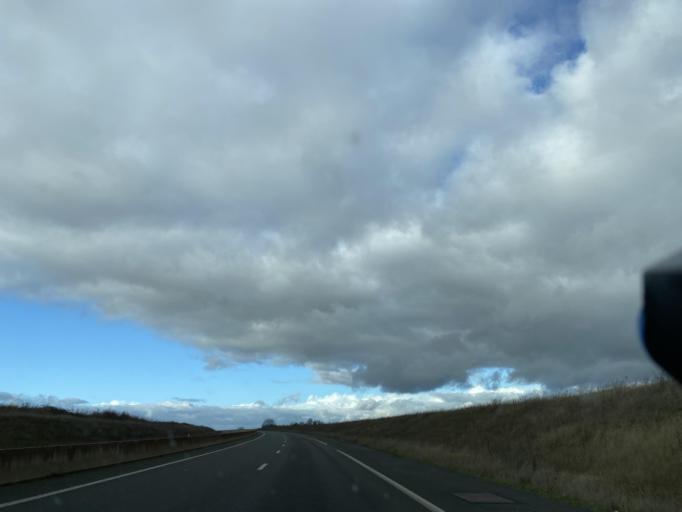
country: FR
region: Centre
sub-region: Departement d'Eure-et-Loir
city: Janville
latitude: 48.2635
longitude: 1.7619
